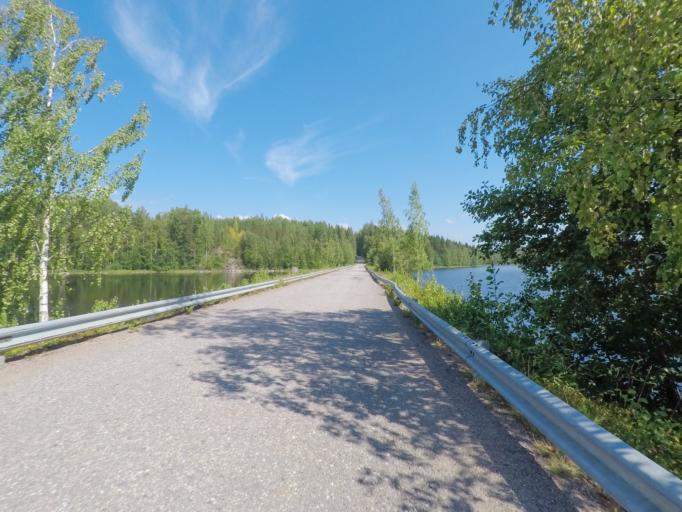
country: FI
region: Southern Savonia
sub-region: Mikkeli
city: Puumala
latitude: 61.4056
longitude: 28.0771
